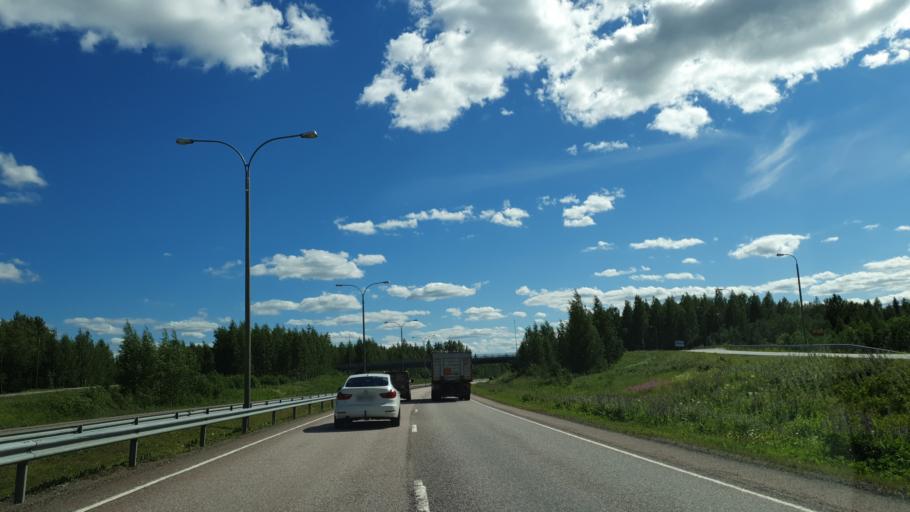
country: FI
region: Northern Savo
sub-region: Varkaus
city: Varkaus
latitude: 62.2890
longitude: 27.8725
